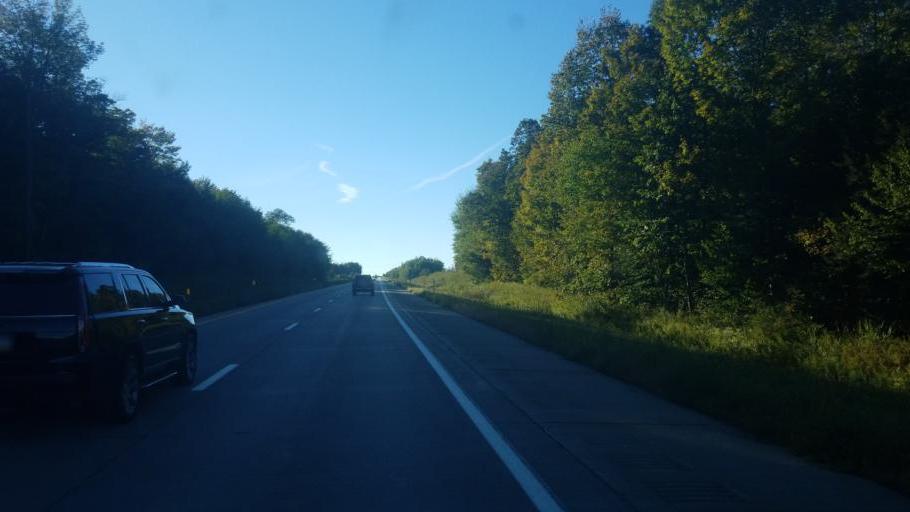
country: US
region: New York
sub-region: Chautauqua County
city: Mayville
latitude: 42.1543
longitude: -79.5183
